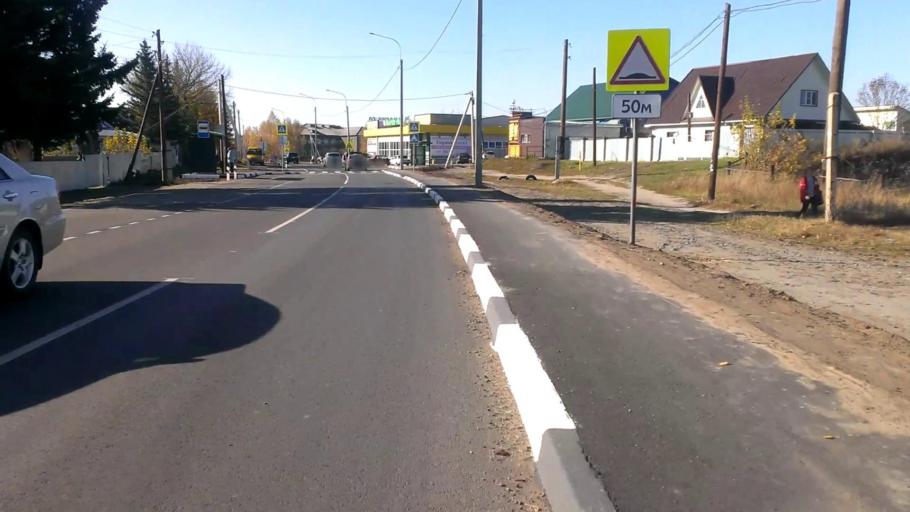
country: RU
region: Altai Krai
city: Sannikovo
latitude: 53.3165
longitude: 83.9576
